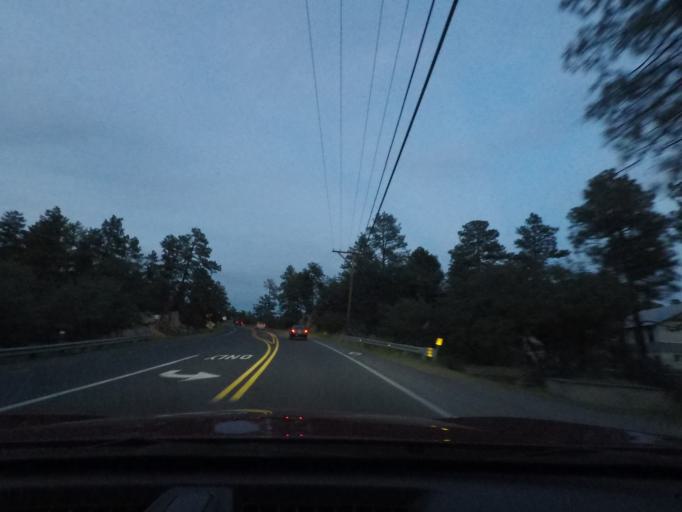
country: US
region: Arizona
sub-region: Yavapai County
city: Prescott
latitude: 34.5704
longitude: -112.5069
